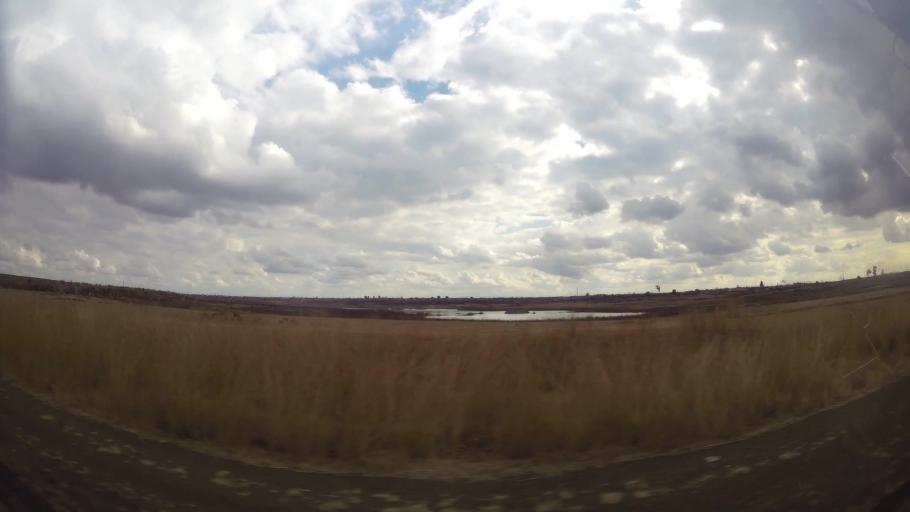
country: ZA
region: Orange Free State
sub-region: Fezile Dabi District Municipality
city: Sasolburg
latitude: -26.8698
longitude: 27.8874
